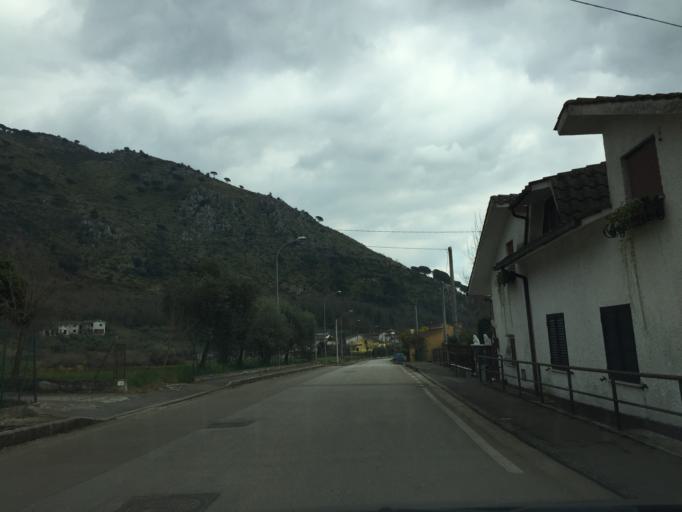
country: IT
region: Latium
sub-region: Provincia di Frosinone
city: Villa Santa Lucia
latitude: 41.4941
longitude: 13.7771
